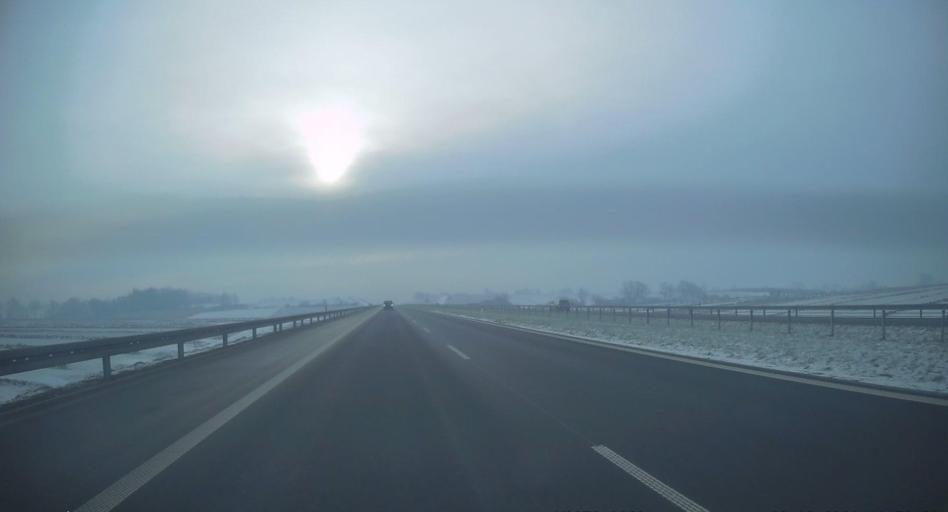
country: PL
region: Lesser Poland Voivodeship
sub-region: Powiat krakowski
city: Slomniki
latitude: 50.2799
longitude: 20.0221
